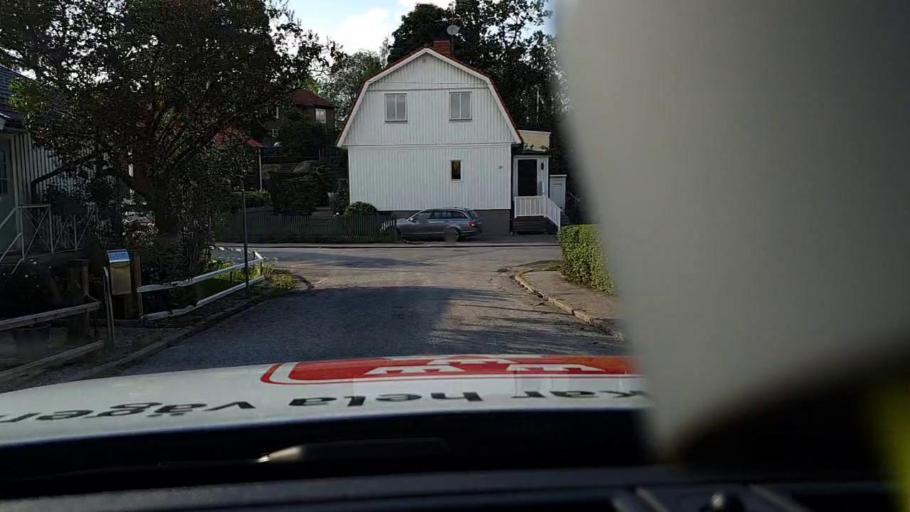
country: SE
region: Stockholm
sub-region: Huddinge Kommun
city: Huddinge
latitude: 59.2721
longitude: 17.9753
